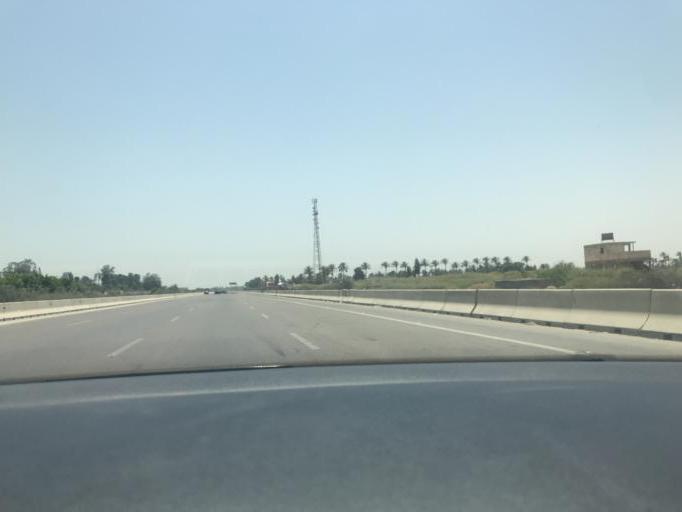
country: EG
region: Alexandria
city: Alexandria
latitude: 30.9327
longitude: 29.8516
